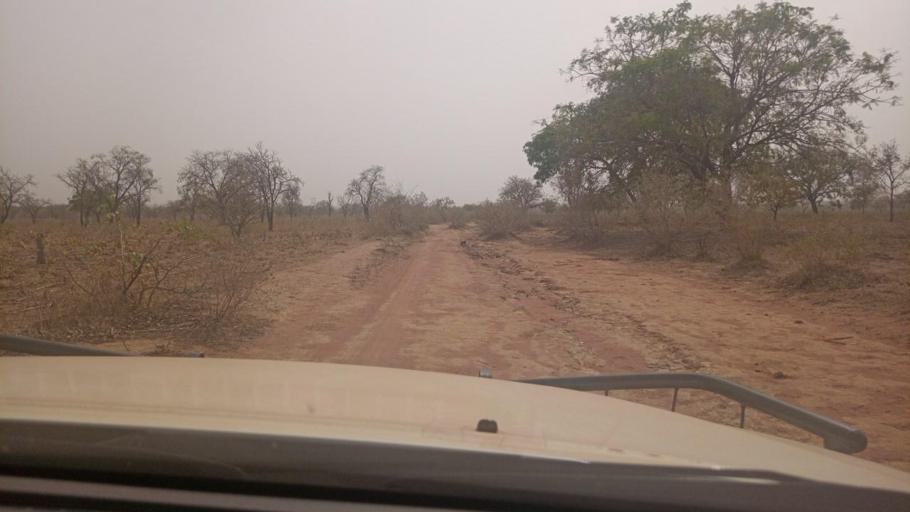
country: BF
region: Boucle du Mouhoun
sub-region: Province des Banwa
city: Salanso
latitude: 12.1650
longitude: -4.2367
